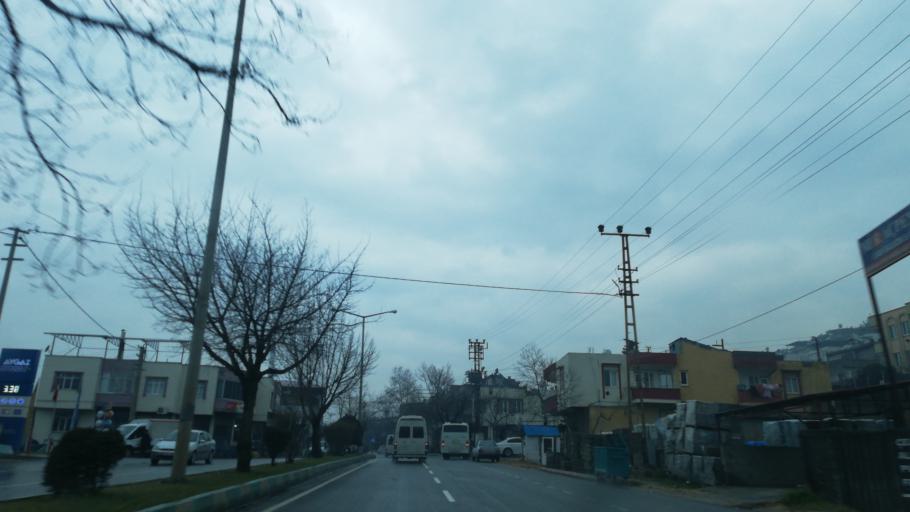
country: TR
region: Kahramanmaras
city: Kahramanmaras
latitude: 37.5824
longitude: 36.9508
